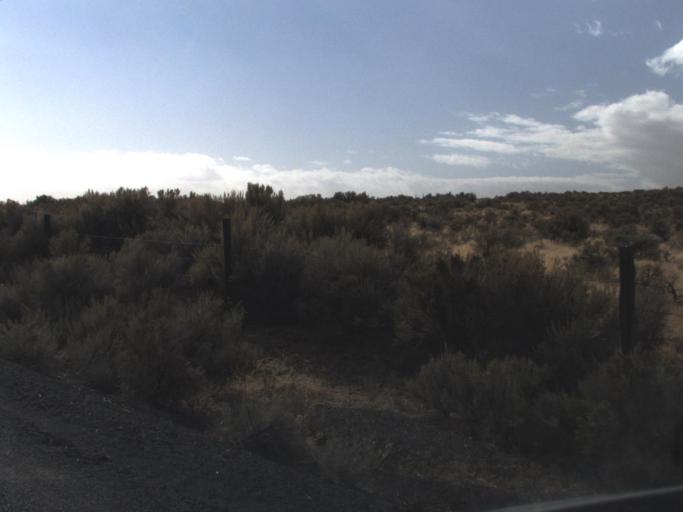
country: US
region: Washington
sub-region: Adams County
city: Ritzville
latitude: 47.4076
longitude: -118.6841
